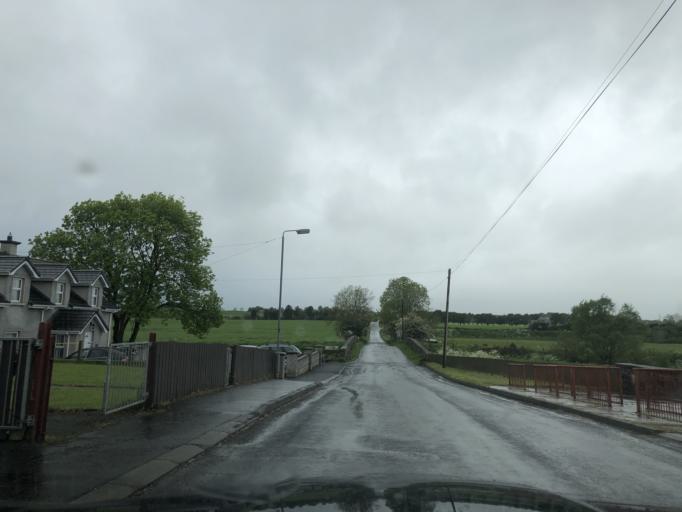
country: GB
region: Northern Ireland
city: Dunloy
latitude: 55.1236
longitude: -6.3631
